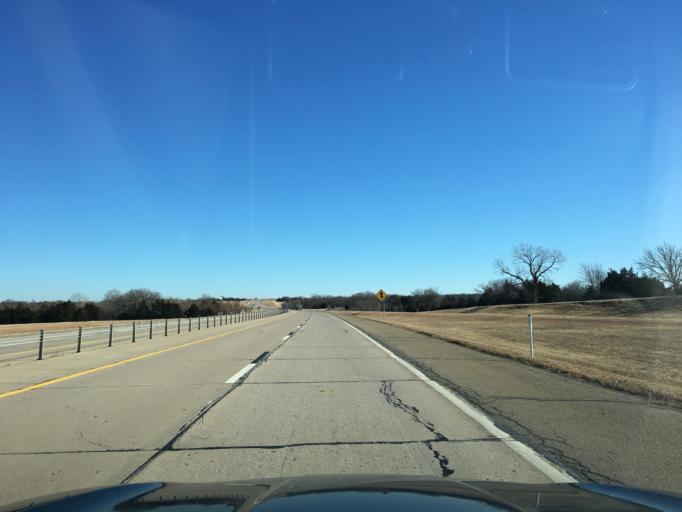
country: US
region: Oklahoma
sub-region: Payne County
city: Stillwater
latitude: 36.2408
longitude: -96.9475
